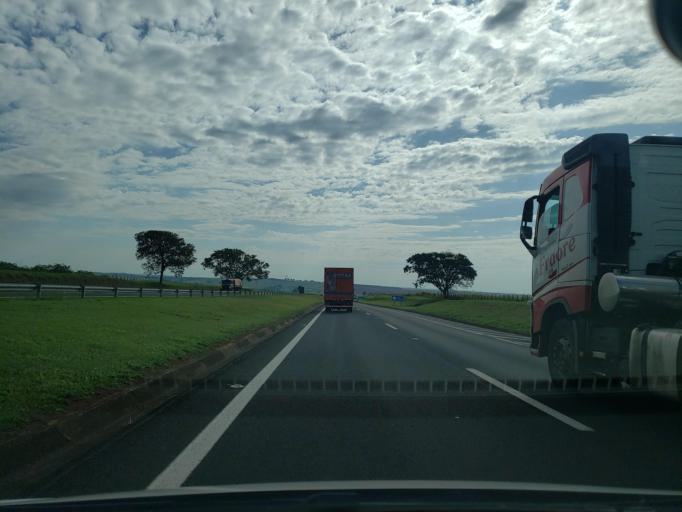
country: BR
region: Sao Paulo
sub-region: Lins
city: Lins
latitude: -21.6633
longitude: -49.7931
